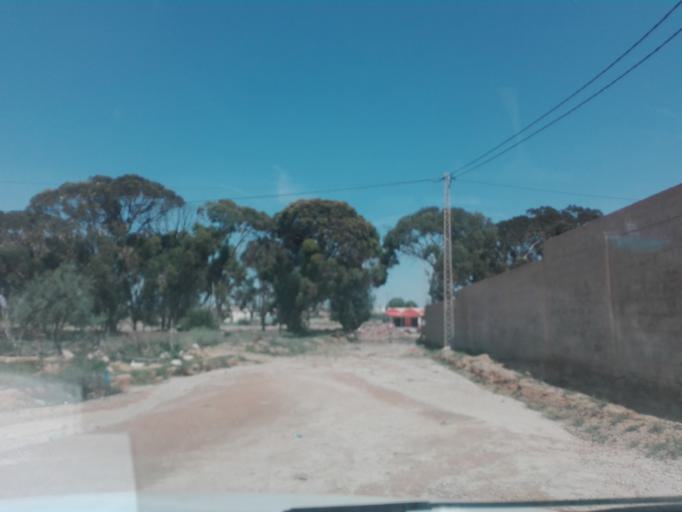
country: TN
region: Safaqis
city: Sfax
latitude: 34.7295
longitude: 10.5193
